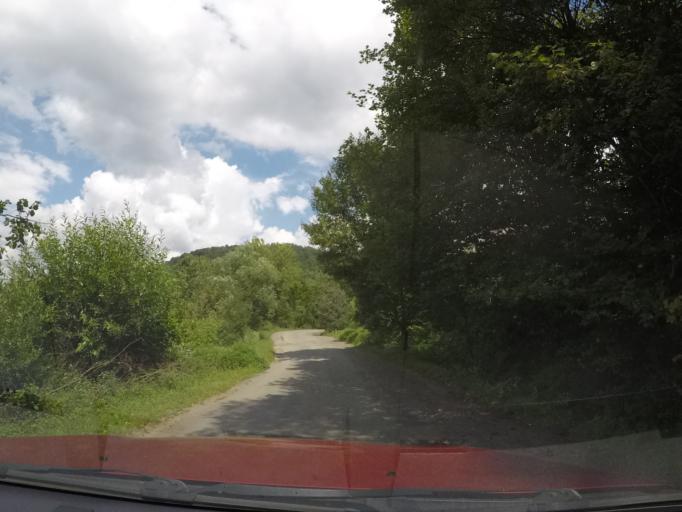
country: UA
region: Zakarpattia
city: Velykyi Bereznyi
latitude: 49.0063
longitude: 22.6385
